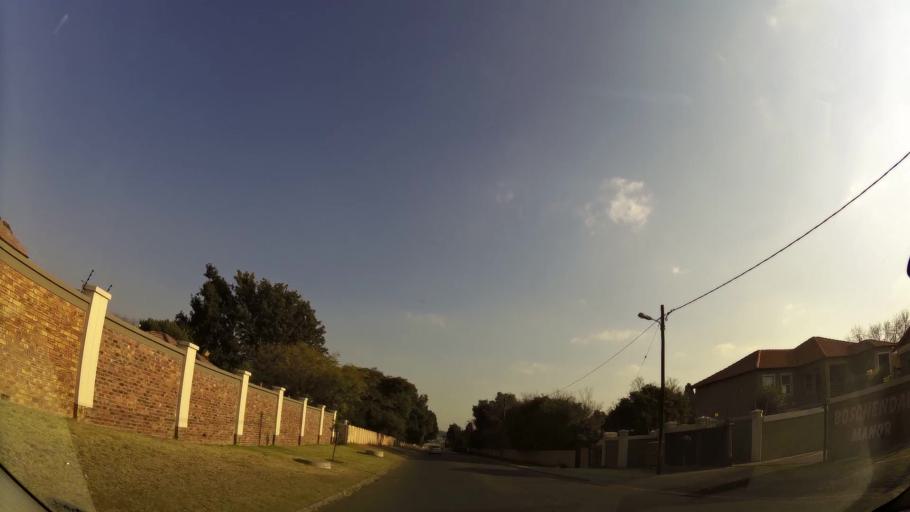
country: ZA
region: Gauteng
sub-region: Ekurhuleni Metropolitan Municipality
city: Benoni
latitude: -26.1400
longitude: 28.3601
